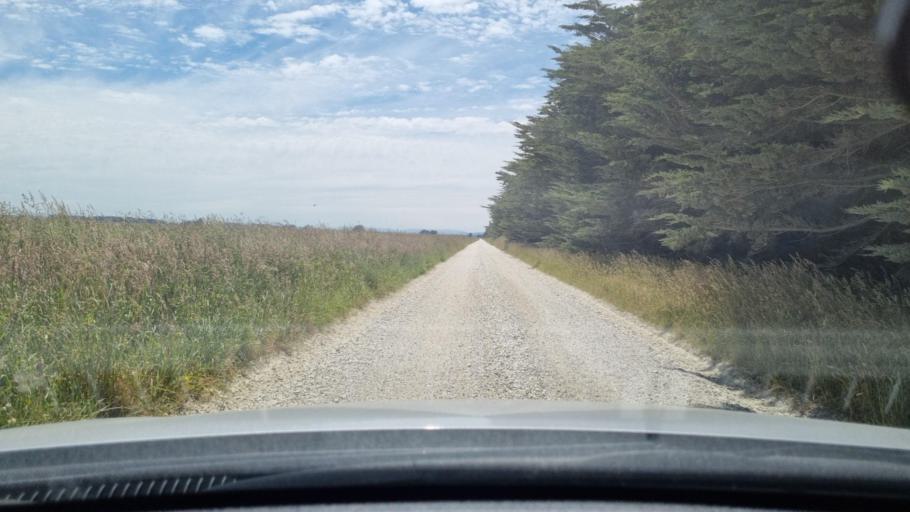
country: NZ
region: Southland
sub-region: Invercargill City
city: Invercargill
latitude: -46.3858
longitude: 168.2648
